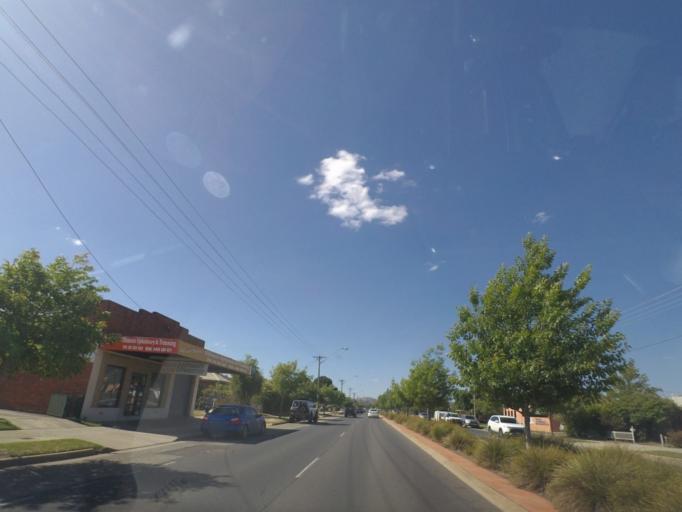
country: AU
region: New South Wales
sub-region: Albury Municipality
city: North Albury
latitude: -36.0594
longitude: 146.9322
